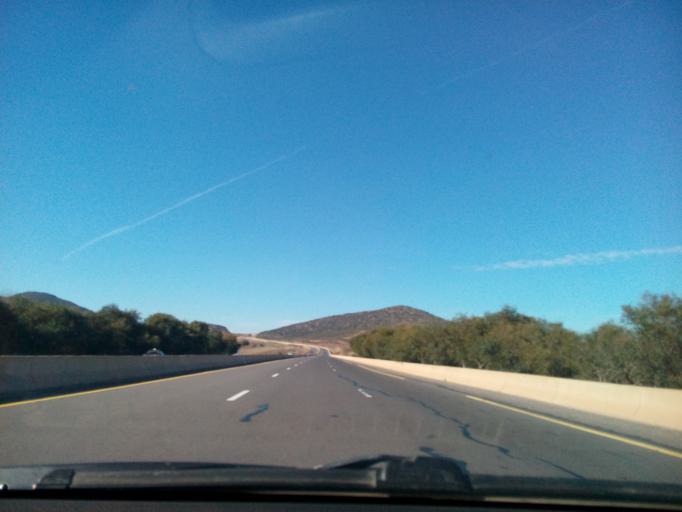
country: DZ
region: Tlemcen
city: Sidi Abdelli
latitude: 35.0192
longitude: -1.1084
